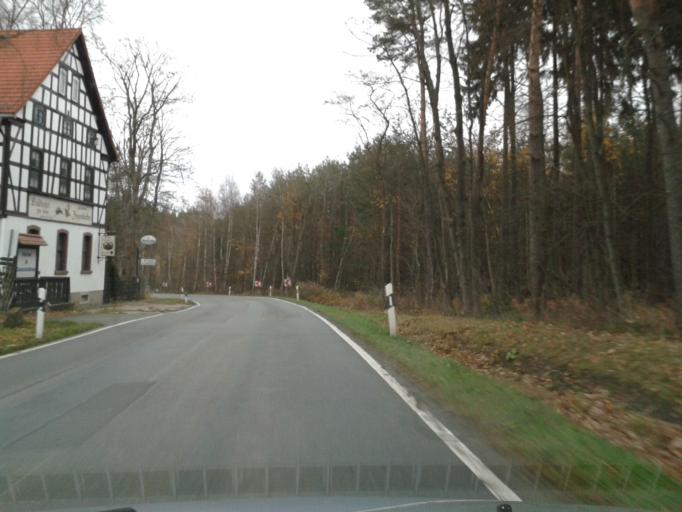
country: DE
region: Thuringia
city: Hainspitz
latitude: 50.9285
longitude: 11.8308
